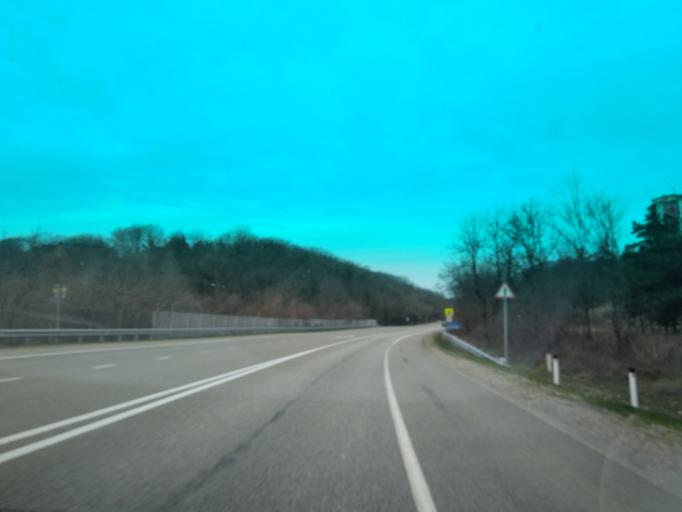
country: RU
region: Krasnodarskiy
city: Ol'ginka
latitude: 44.1873
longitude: 38.8928
